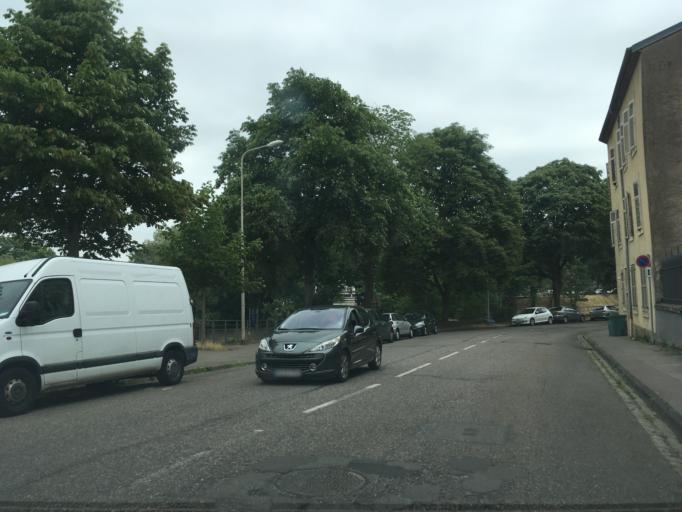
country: FR
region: Lorraine
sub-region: Departement de Meurthe-et-Moselle
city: Saint-Max
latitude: 48.6994
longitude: 6.1940
